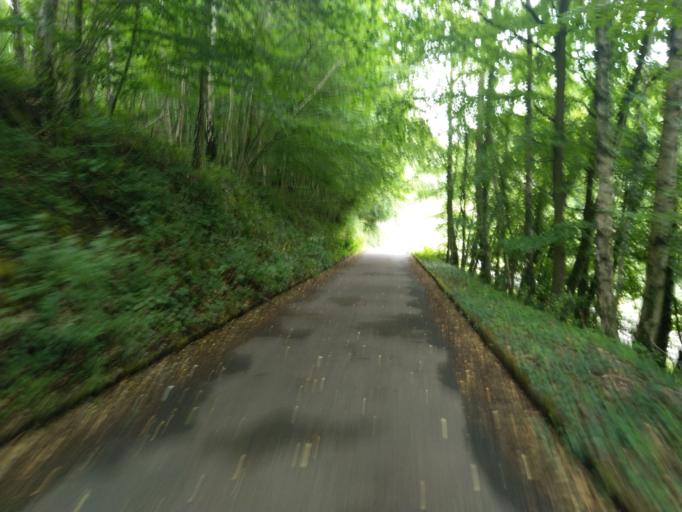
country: BE
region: Wallonia
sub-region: Province du Hainaut
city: Bernissart
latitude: 50.5000
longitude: 3.6390
